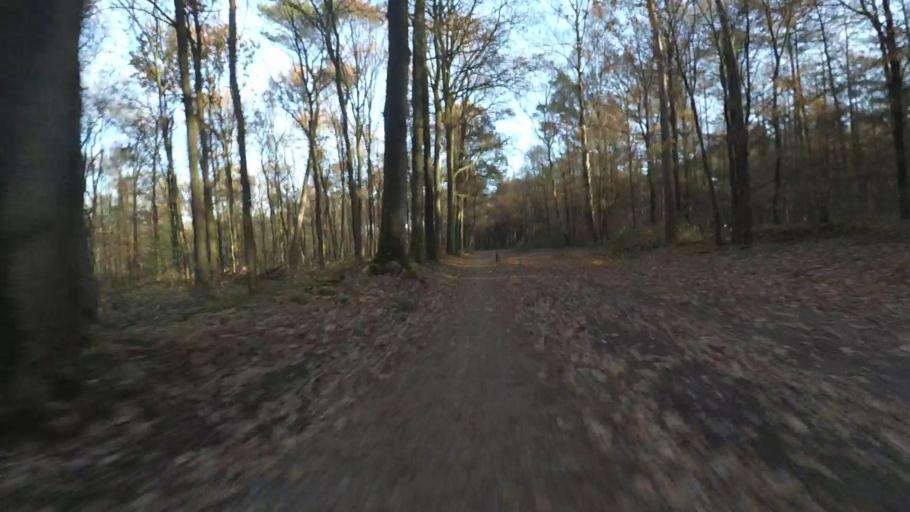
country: NL
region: Utrecht
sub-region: Gemeente Utrechtse Heuvelrug
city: Overberg
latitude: 52.0097
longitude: 5.5141
